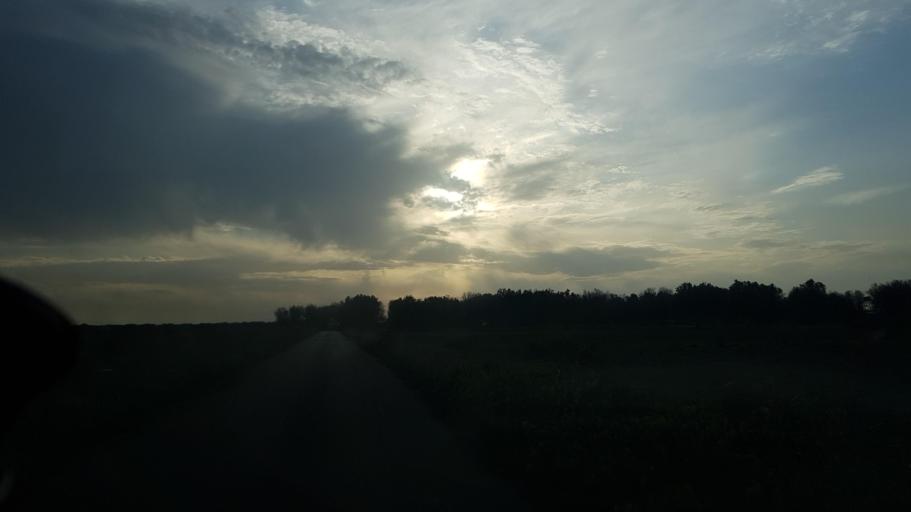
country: IT
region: Apulia
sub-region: Provincia di Brindisi
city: Mesagne
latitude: 40.5228
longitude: 17.8302
